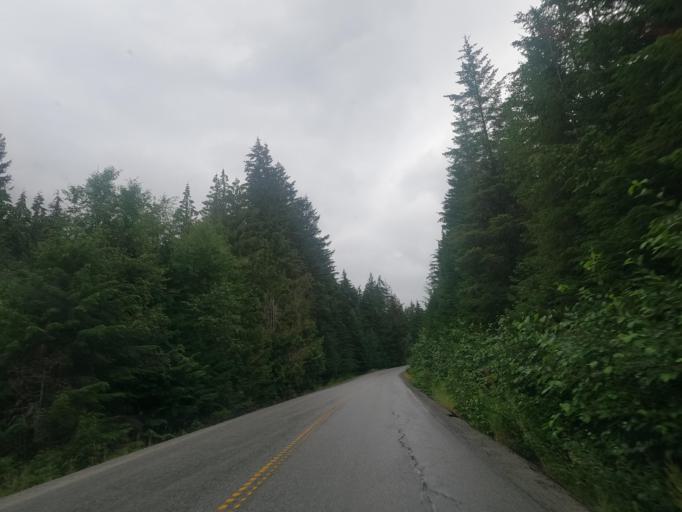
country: CA
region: British Columbia
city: Pemberton
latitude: 50.3183
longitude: -122.5635
